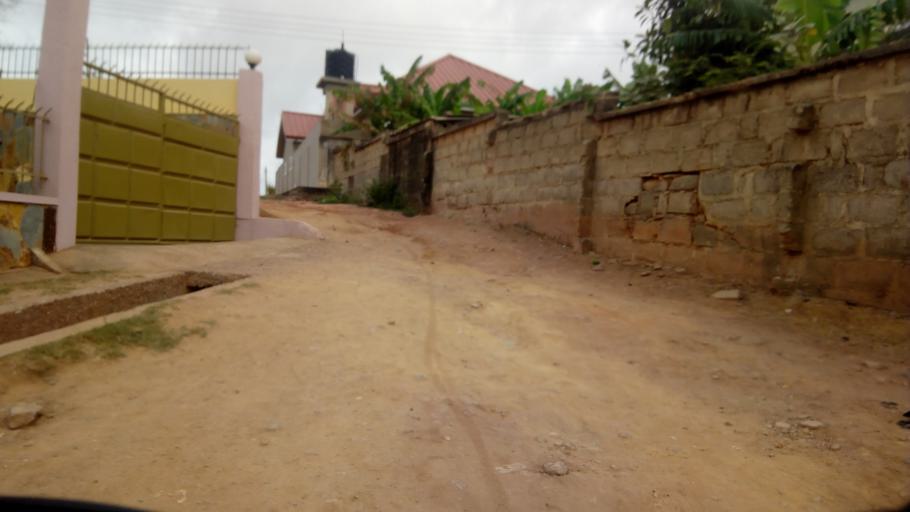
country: GH
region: Central
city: Cape Coast
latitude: 5.1201
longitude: -1.2686
